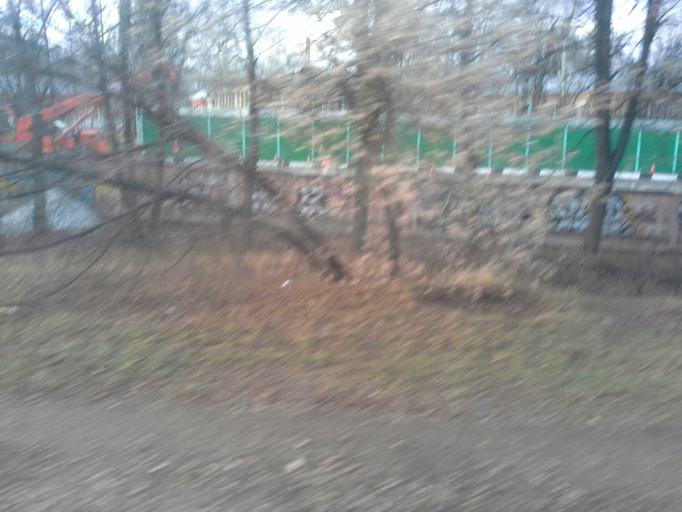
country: RU
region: Moskovskaya
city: Cherkizovo
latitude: 55.9287
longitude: 37.7778
